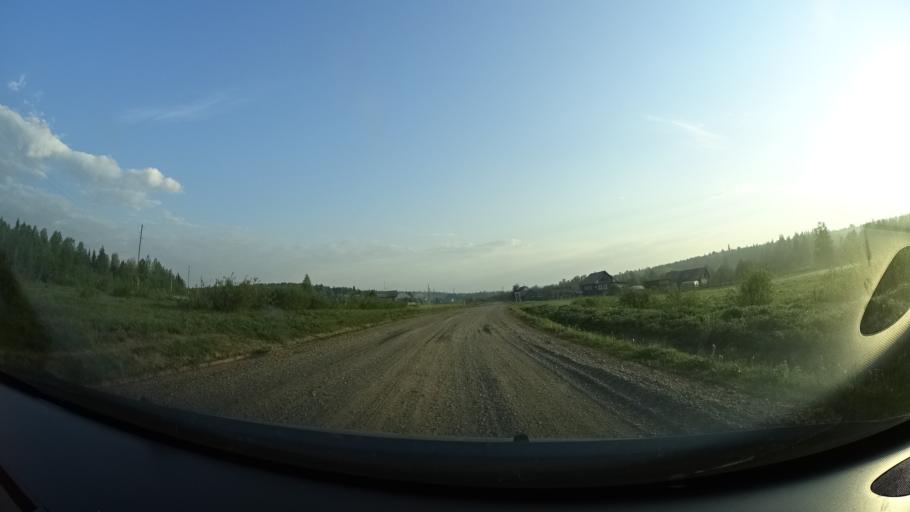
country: RU
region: Perm
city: Kuyeda
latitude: 56.6112
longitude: 55.7110
